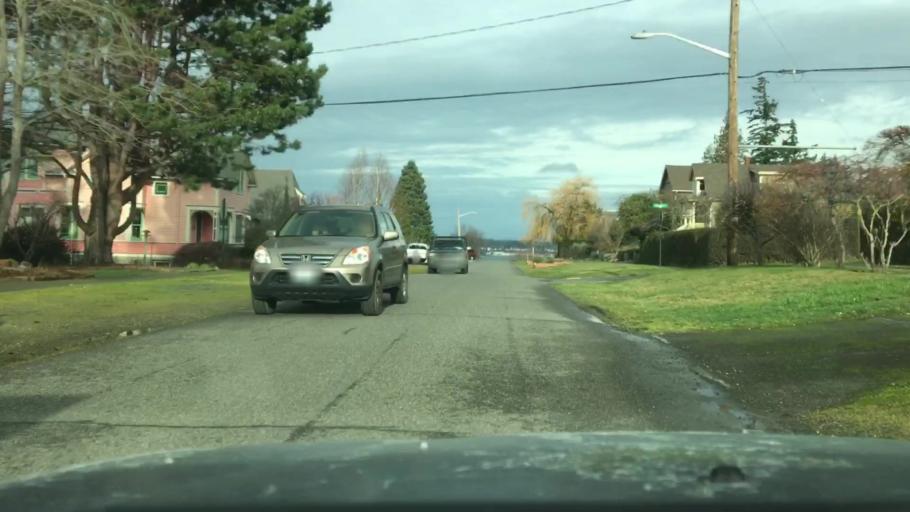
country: US
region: Washington
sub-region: Whatcom County
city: Bellingham
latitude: 48.7272
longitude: -122.5015
